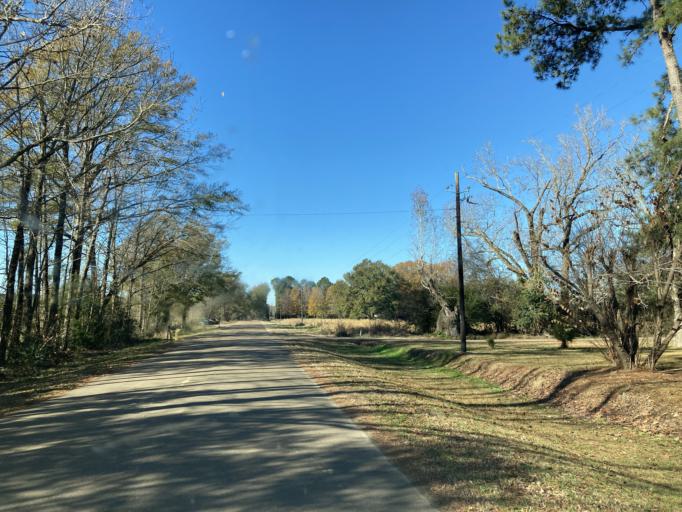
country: US
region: Mississippi
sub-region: Madison County
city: Kearney Park
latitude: 32.6040
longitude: -90.4026
